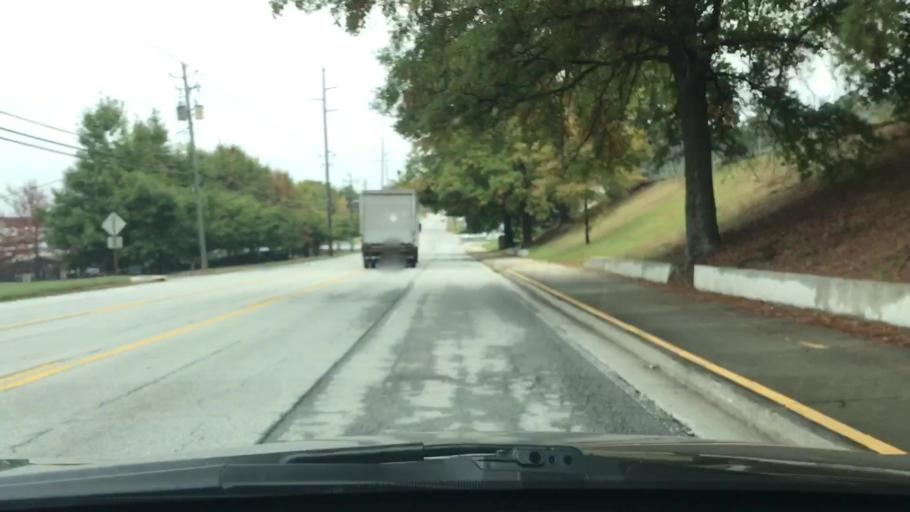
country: US
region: Georgia
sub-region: DeKalb County
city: Avondale Estates
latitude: 33.7801
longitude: -84.2752
